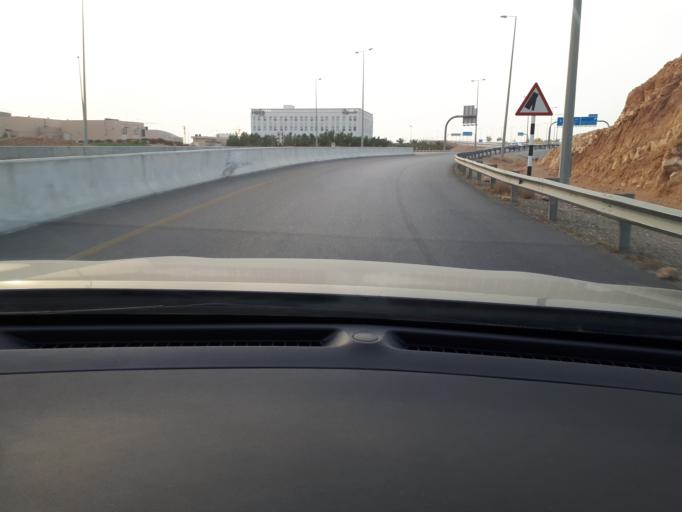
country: OM
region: Muhafazat Masqat
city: Bawshar
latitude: 23.5638
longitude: 58.3391
